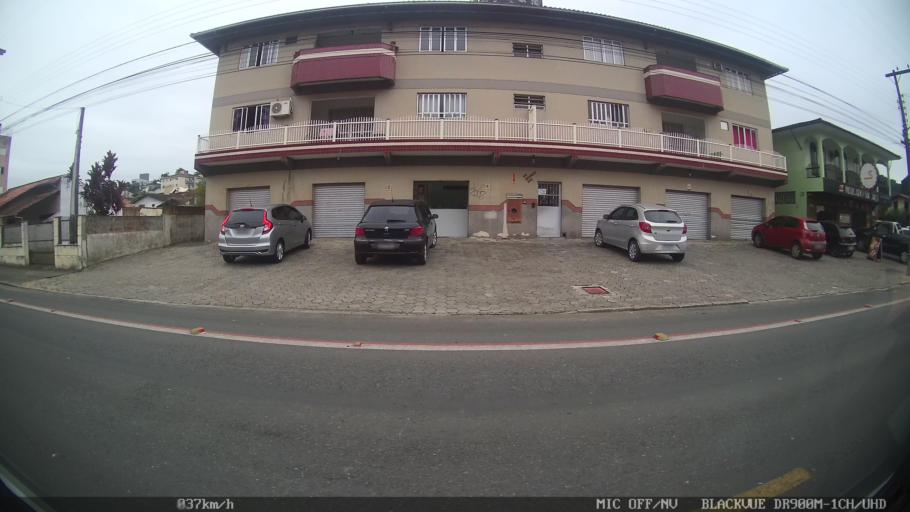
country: BR
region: Santa Catarina
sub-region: Joinville
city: Joinville
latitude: -26.2783
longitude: -48.8403
